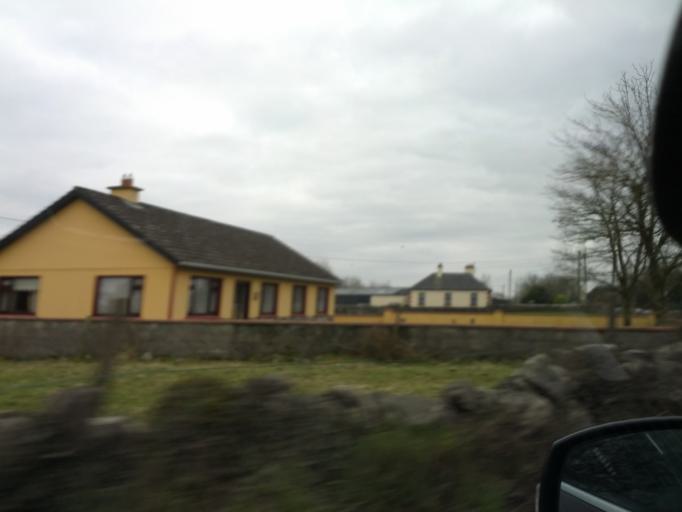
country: IE
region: Connaught
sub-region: County Galway
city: Athenry
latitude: 53.2567
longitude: -8.7393
